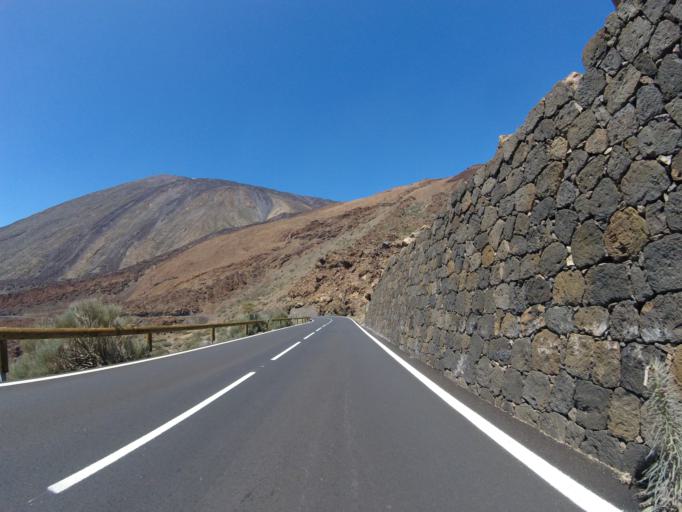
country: ES
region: Canary Islands
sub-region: Provincia de Santa Cruz de Tenerife
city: Vilaflor
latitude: 28.2582
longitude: -16.6128
